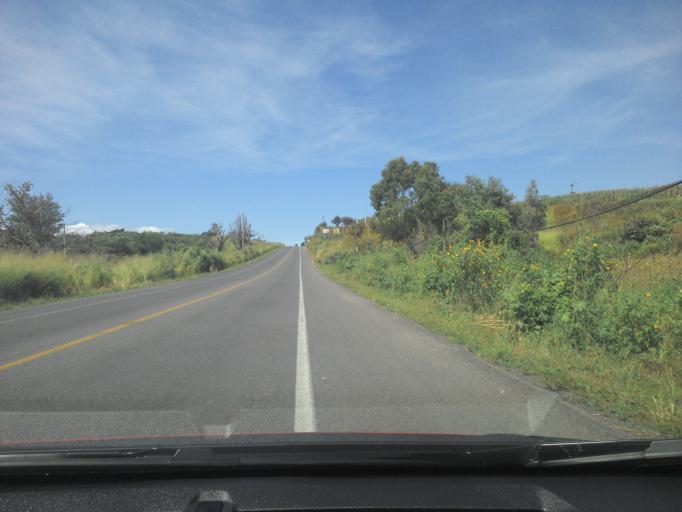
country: MX
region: Jalisco
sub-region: Teuchitlan
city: La Estanzuela
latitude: 20.6757
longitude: -103.8332
